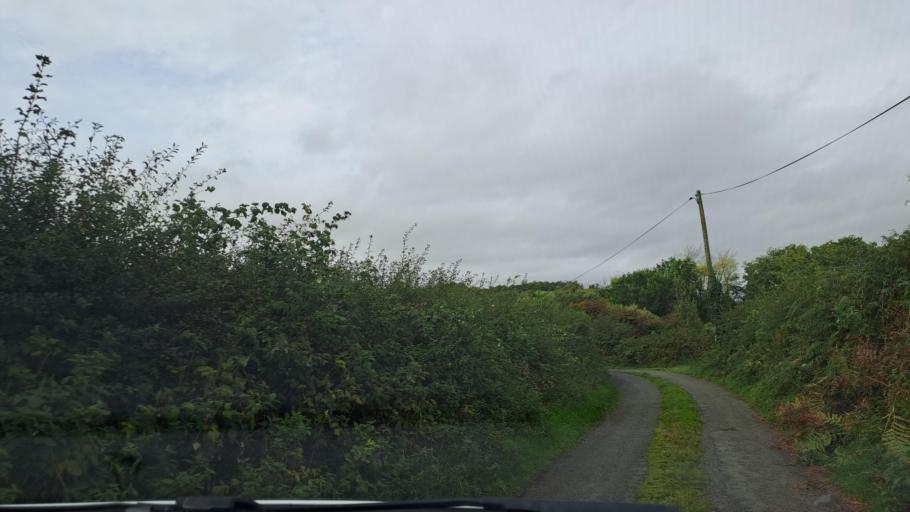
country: IE
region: Ulster
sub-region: An Cabhan
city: Bailieborough
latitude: 54.0050
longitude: -6.9514
